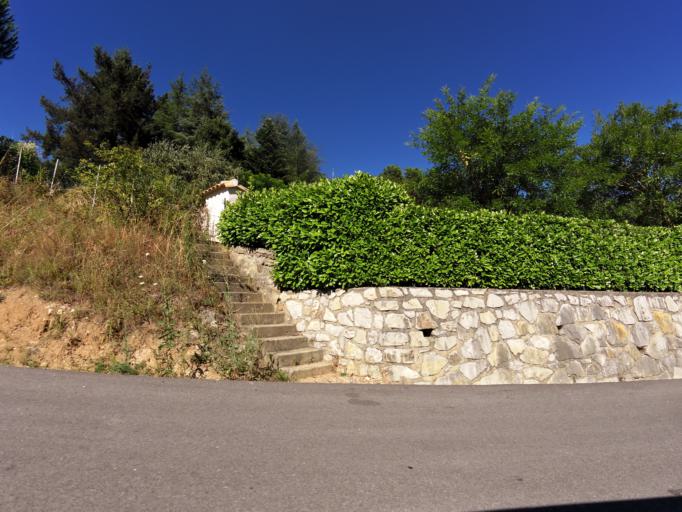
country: FR
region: Languedoc-Roussillon
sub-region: Departement du Gard
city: Saint-Jean-du-Gard
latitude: 44.1022
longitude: 3.8946
